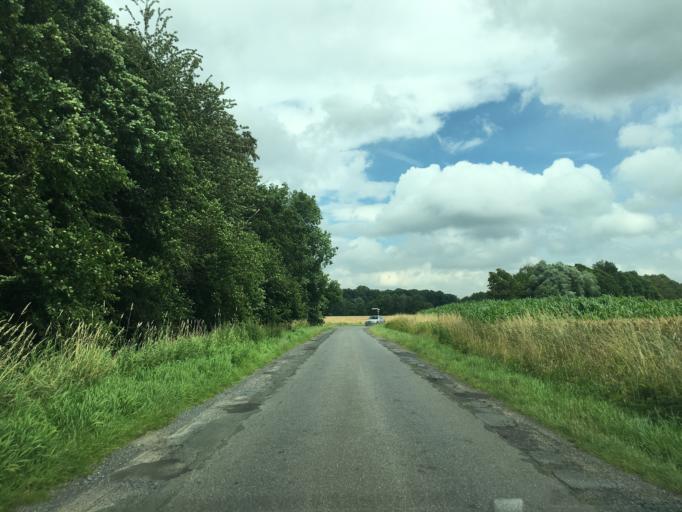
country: DE
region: North Rhine-Westphalia
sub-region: Regierungsbezirk Munster
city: Greven
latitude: 52.0373
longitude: 7.5996
